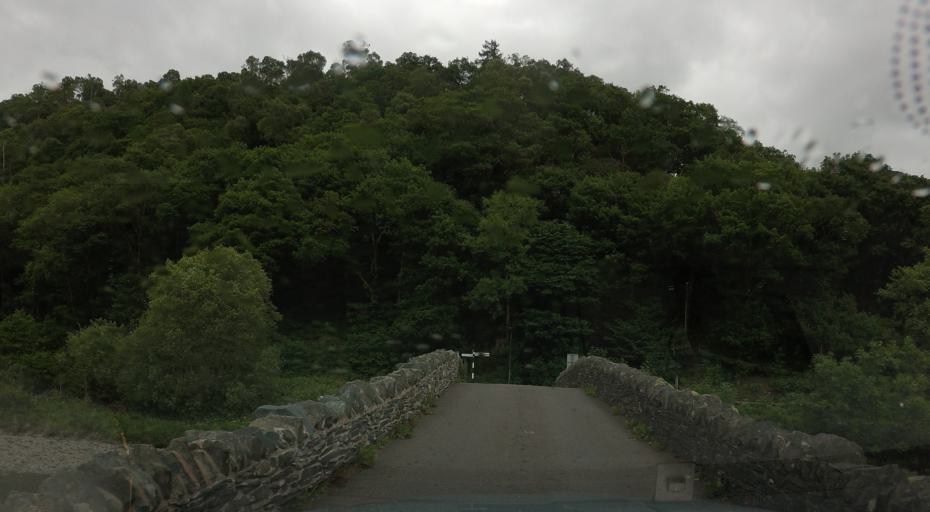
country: GB
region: England
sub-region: Cumbria
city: Keswick
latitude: 54.5468
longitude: -3.1545
